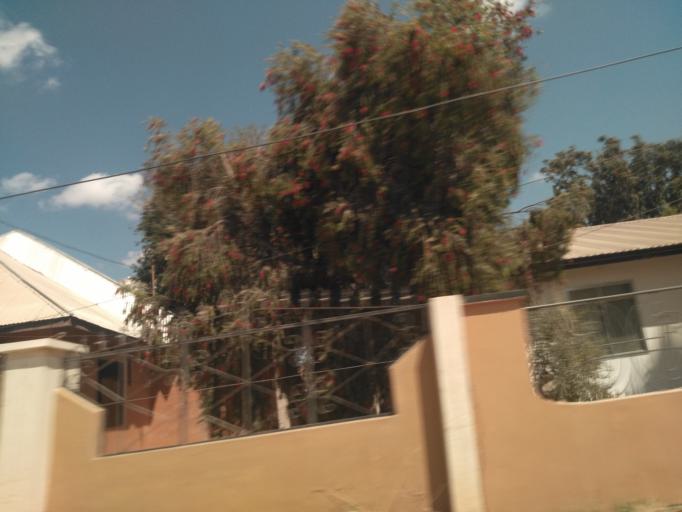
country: TZ
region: Dodoma
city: Dodoma
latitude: -6.1682
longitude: 35.7632
